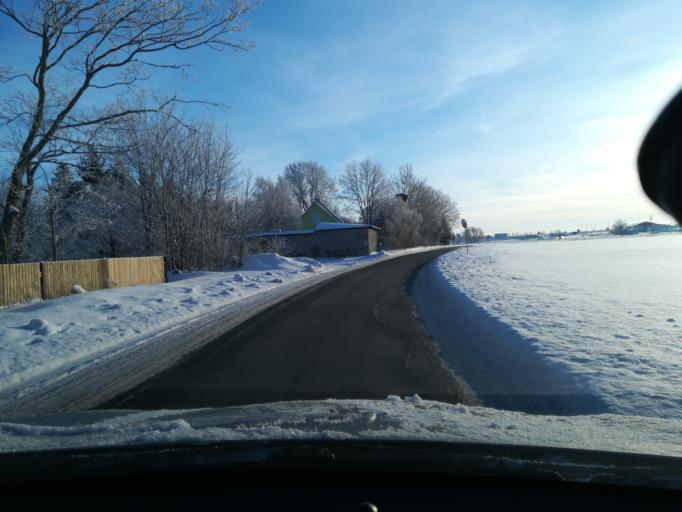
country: EE
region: Harju
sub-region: Saue linn
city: Saue
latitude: 59.3549
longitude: 24.5576
